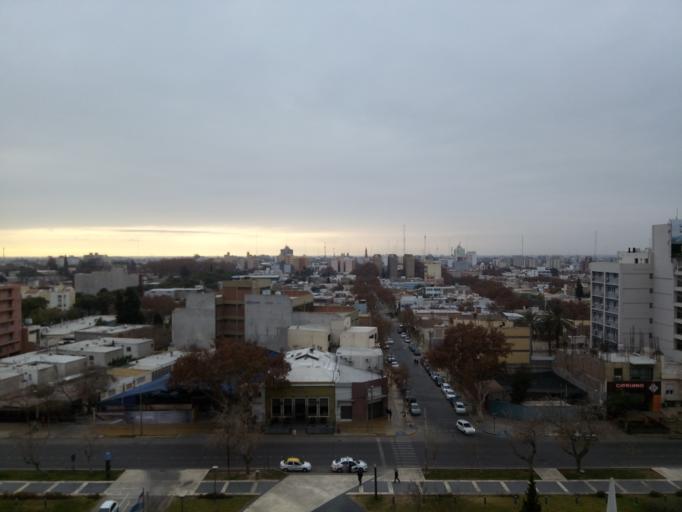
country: AR
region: San Juan
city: San Juan
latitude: -31.5369
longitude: -68.5368
